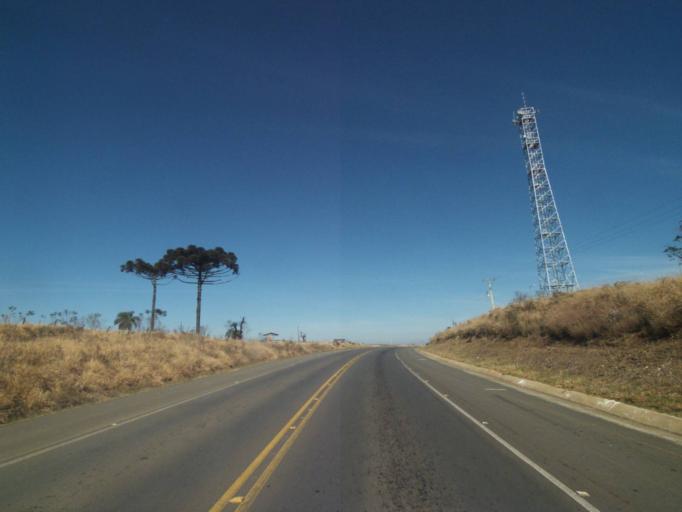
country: BR
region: Parana
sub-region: Tibagi
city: Tibagi
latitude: -24.7993
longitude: -50.4673
